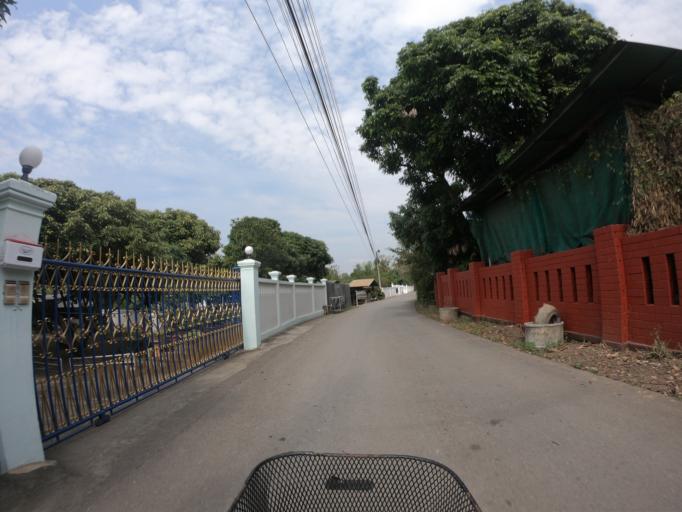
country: TH
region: Chiang Mai
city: Saraphi
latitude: 18.7071
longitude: 99.0386
